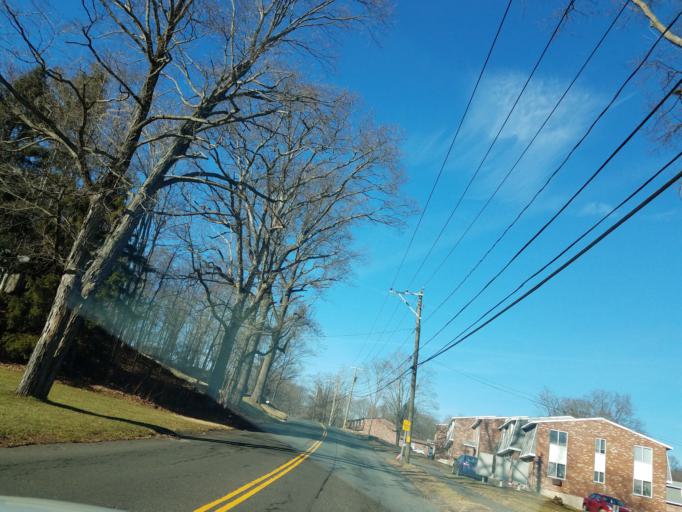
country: US
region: Connecticut
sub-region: New Haven County
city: Meriden
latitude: 41.5373
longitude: -72.8277
